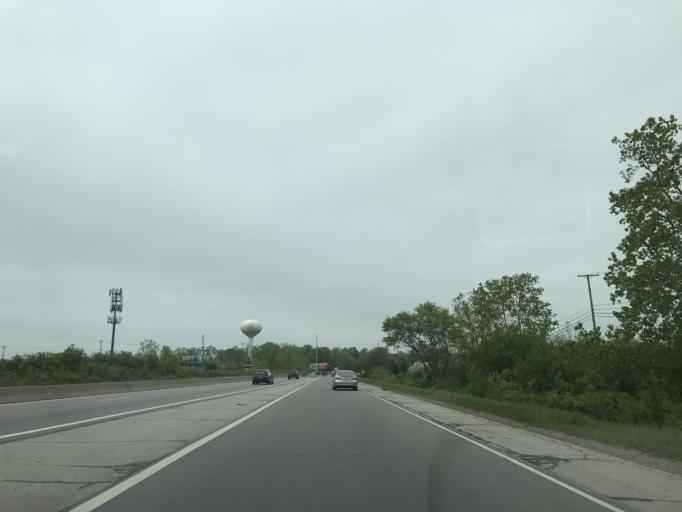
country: US
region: Michigan
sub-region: Washtenaw County
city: Ann Arbor
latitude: 42.2370
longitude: -83.7434
